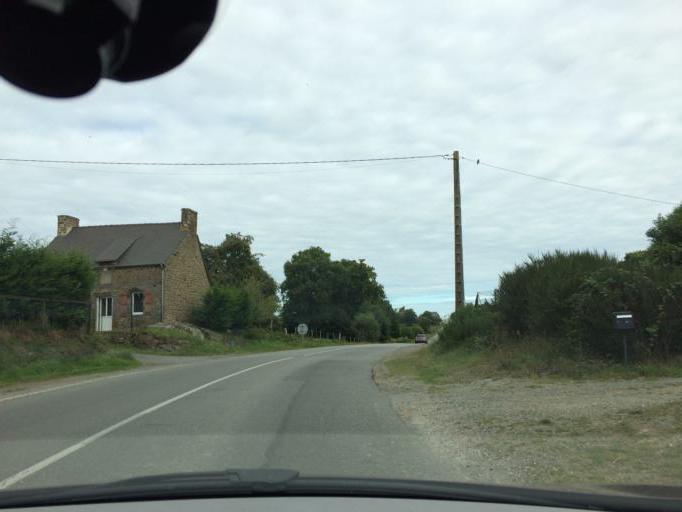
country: FR
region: Brittany
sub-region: Departement d'Ille-et-Vilaine
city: Miniac-Morvan
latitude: 48.4942
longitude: -1.9048
